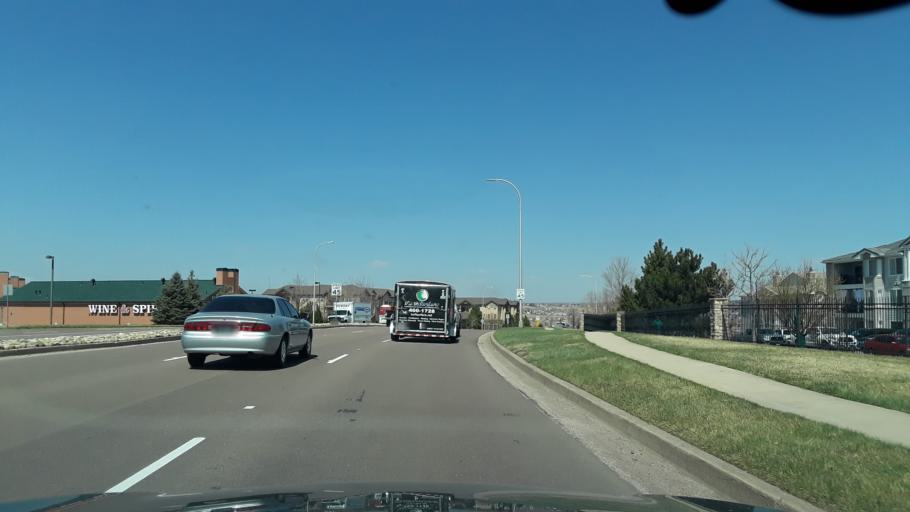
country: US
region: Colorado
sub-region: El Paso County
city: Cimarron Hills
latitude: 38.9206
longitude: -104.7381
